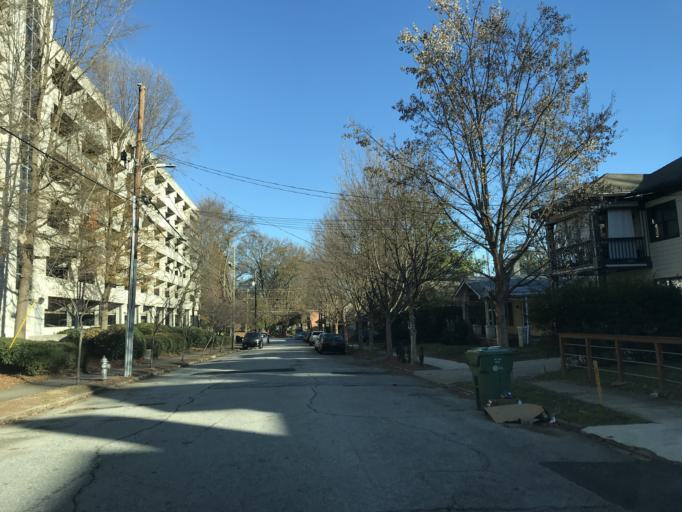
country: US
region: Georgia
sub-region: Fulton County
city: Atlanta
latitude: 33.7621
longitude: -84.3705
